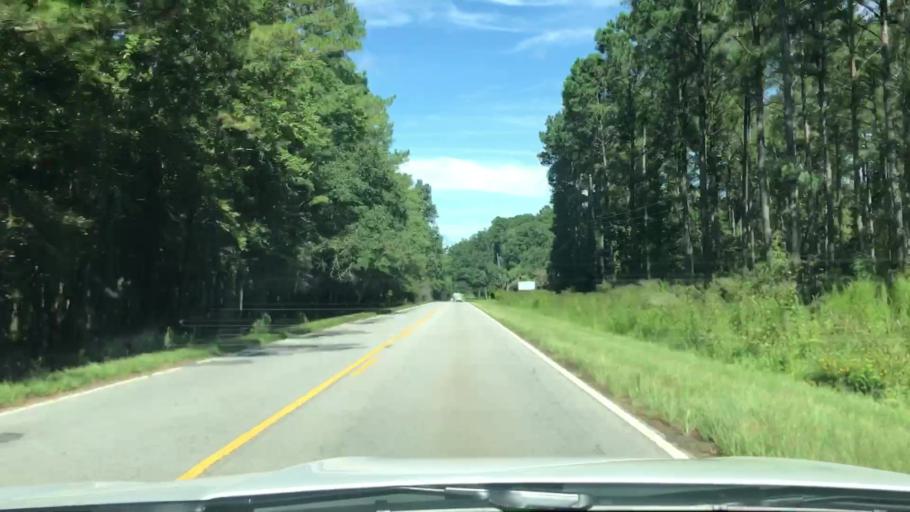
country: US
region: South Carolina
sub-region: Dorchester County
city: Centerville
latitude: 32.9409
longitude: -80.1865
